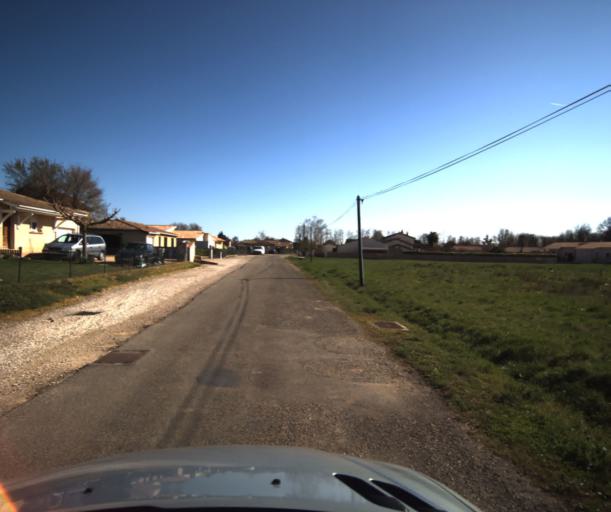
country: FR
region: Midi-Pyrenees
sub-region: Departement du Tarn-et-Garonne
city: Bressols
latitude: 43.9697
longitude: 1.3344
